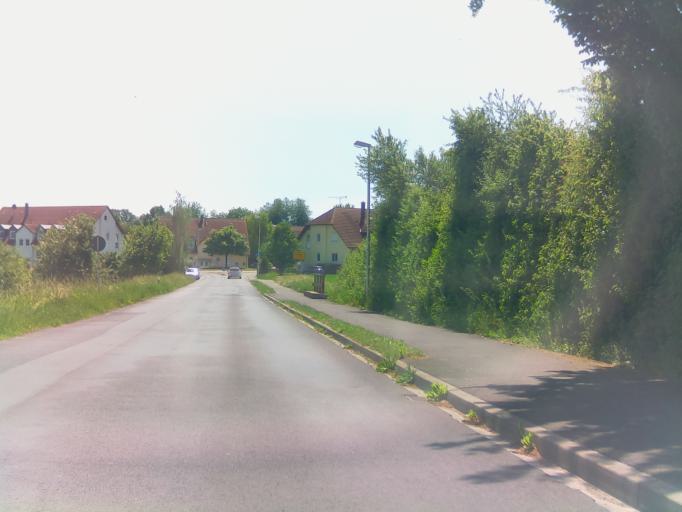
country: DE
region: Bavaria
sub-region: Regierungsbezirk Unterfranken
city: Poppenhausen
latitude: 50.0890
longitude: 10.1420
